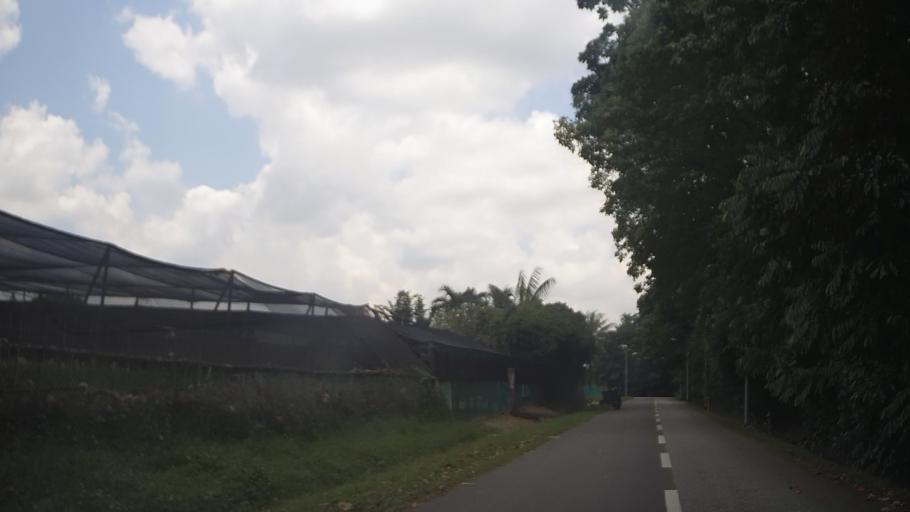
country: MY
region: Johor
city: Kampung Pasir Gudang Baru
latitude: 1.3996
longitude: 103.8662
